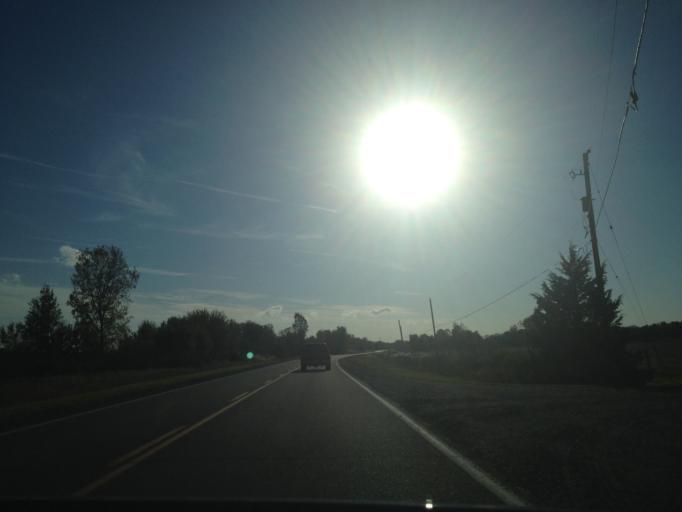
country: CA
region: Ontario
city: Delaware
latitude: 42.6140
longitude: -81.5915
